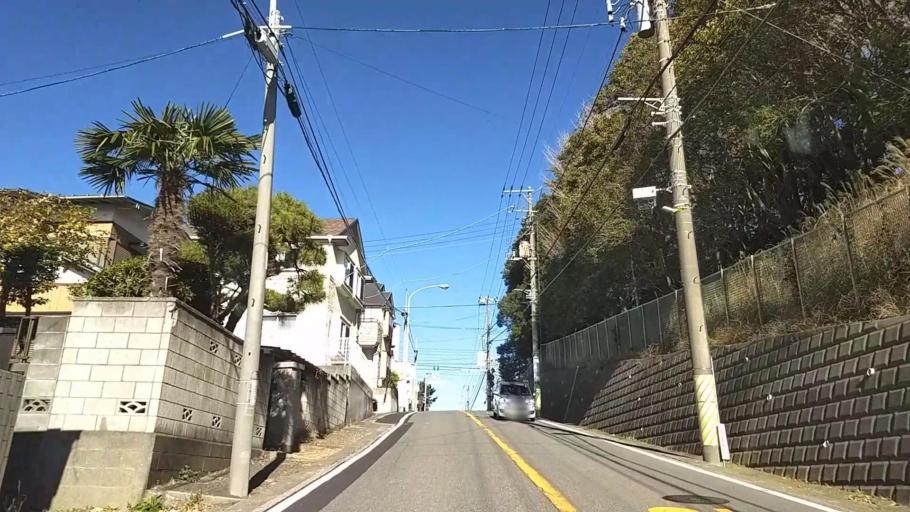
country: JP
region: Kanagawa
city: Yokohama
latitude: 35.4500
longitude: 139.5894
